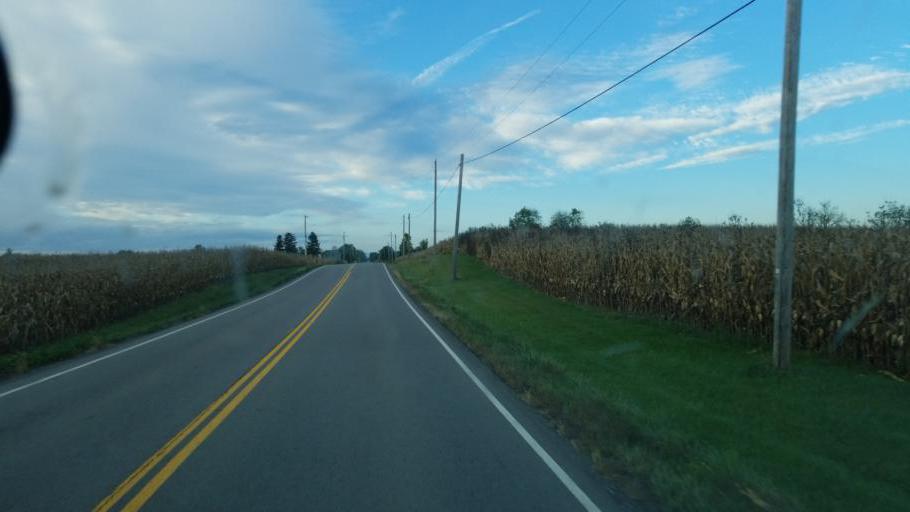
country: US
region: Ohio
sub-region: Licking County
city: Utica
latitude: 40.2339
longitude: -82.5195
